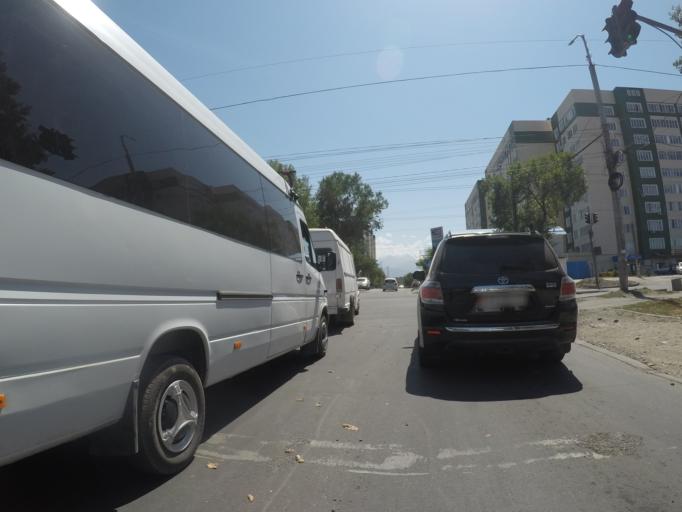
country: KG
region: Chuy
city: Bishkek
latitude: 42.8439
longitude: 74.5768
